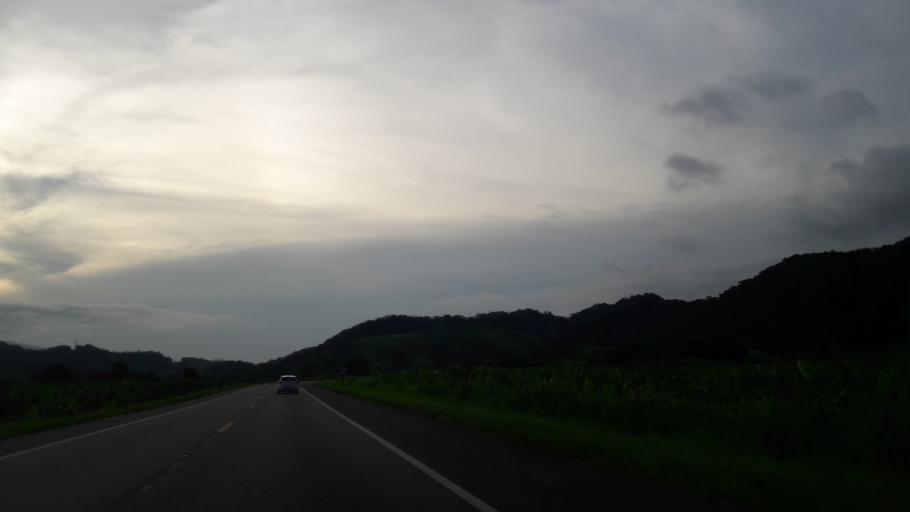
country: BR
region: Sao Paulo
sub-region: Peruibe
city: Peruibe
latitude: -24.2967
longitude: -47.0863
